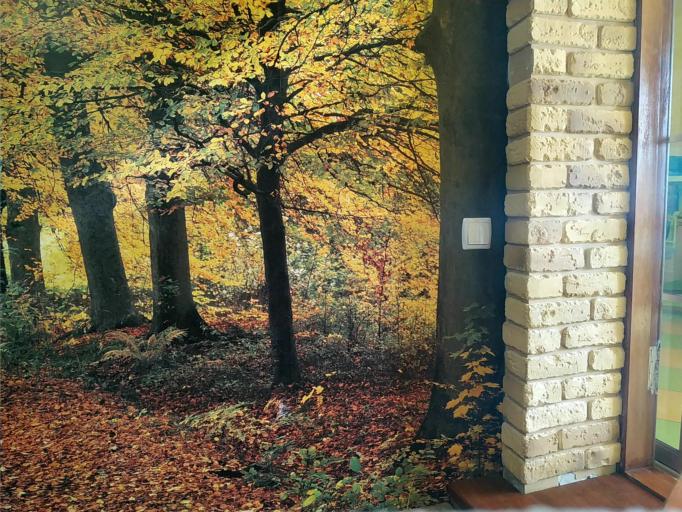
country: RU
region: Smolensk
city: Katyn'
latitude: 55.0072
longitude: 31.7717
